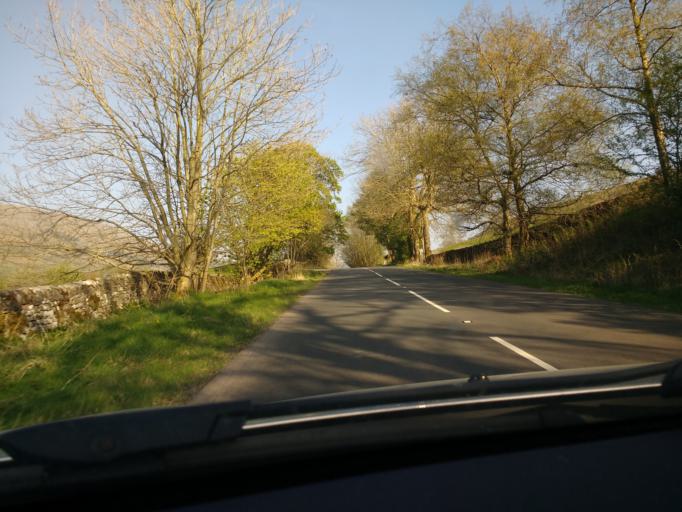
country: GB
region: England
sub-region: Cumbria
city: Sedbergh
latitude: 54.3121
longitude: -2.4551
